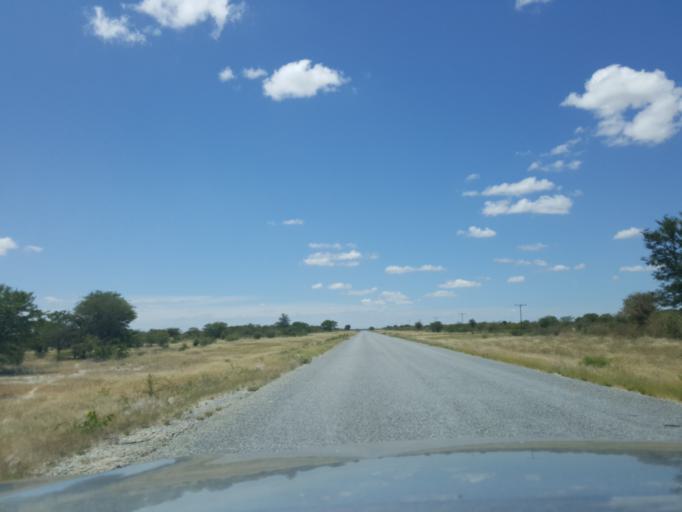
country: BW
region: Central
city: Gweta
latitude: -20.1357
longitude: 25.6567
